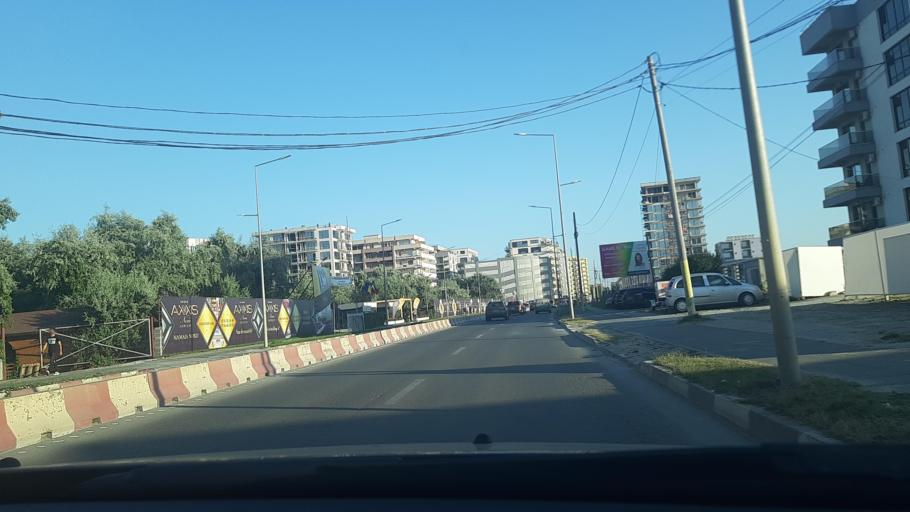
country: RO
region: Constanta
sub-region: Comuna Navodari
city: Navodari
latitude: 44.2755
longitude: 28.6176
